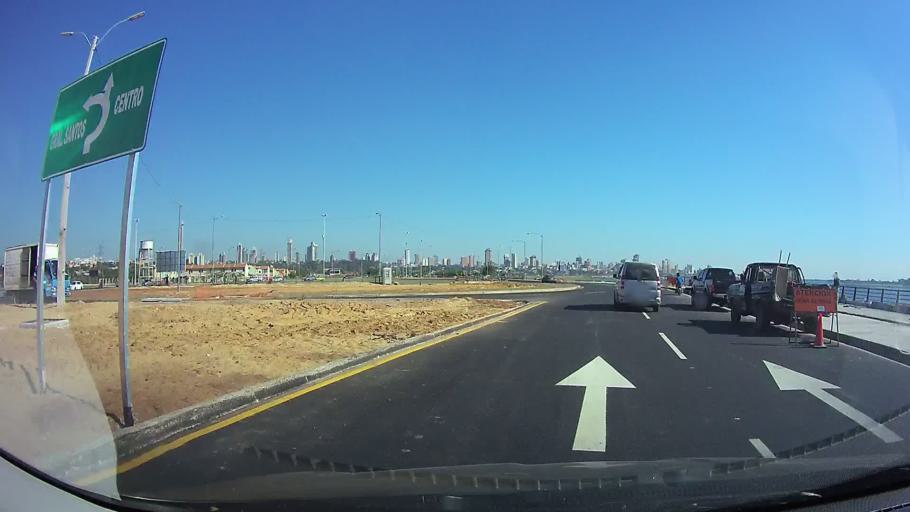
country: PY
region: Asuncion
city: Asuncion
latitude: -25.2694
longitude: -57.6128
